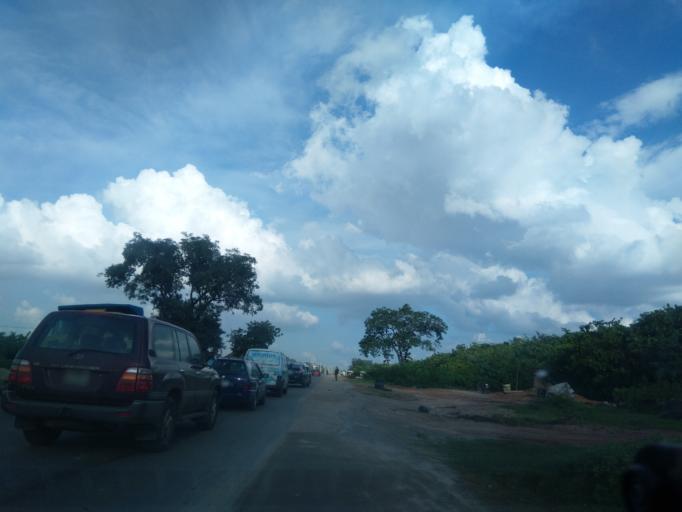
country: NG
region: Abuja Federal Capital Territory
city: Abuja
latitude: 9.0430
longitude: 7.3888
